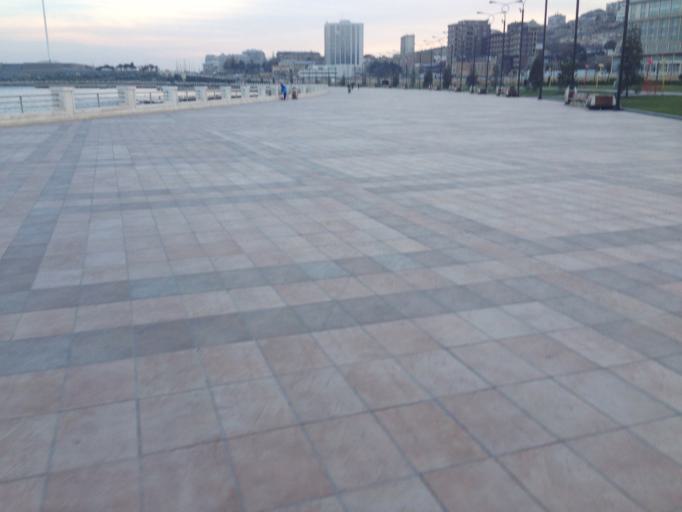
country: AZ
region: Baki
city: Badamdar
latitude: 40.3520
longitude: 49.8368
